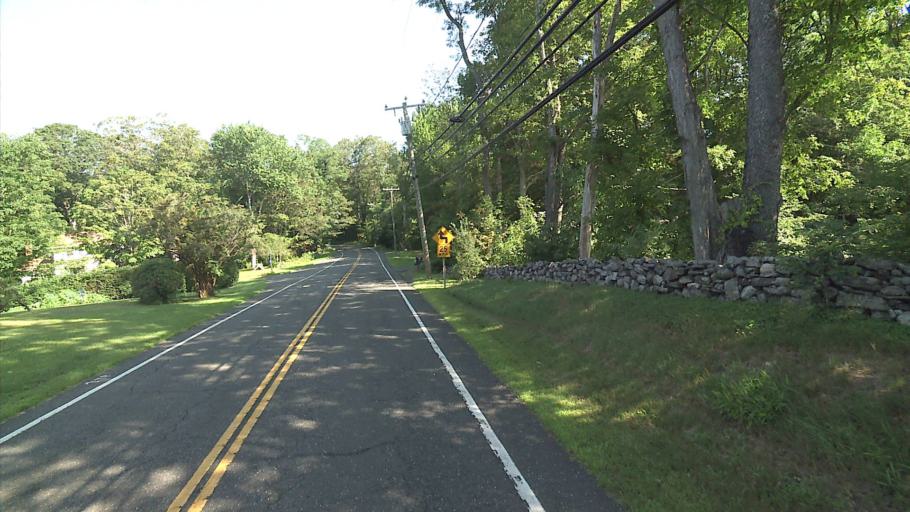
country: US
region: Connecticut
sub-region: Litchfield County
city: Winsted
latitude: 41.9405
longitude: -73.0866
